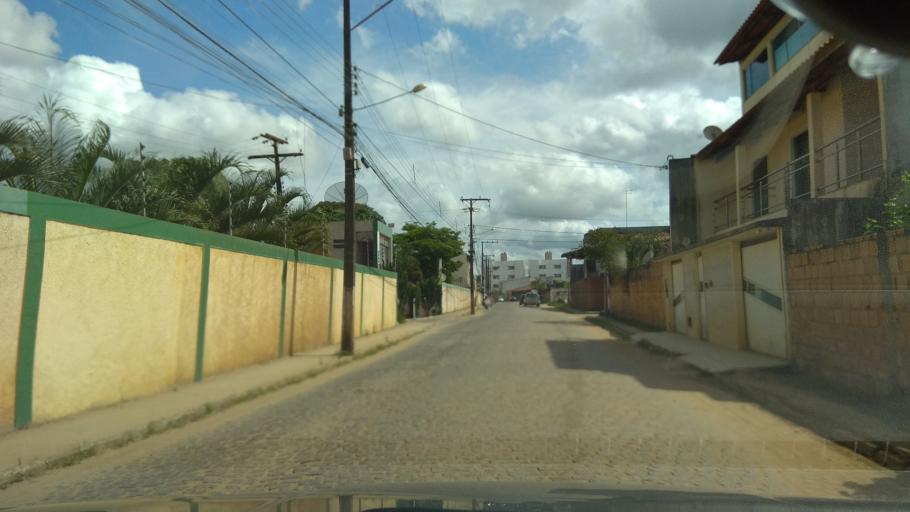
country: BR
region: Bahia
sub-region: Santo Antonio De Jesus
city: Santo Antonio de Jesus
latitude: -12.9792
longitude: -39.2616
